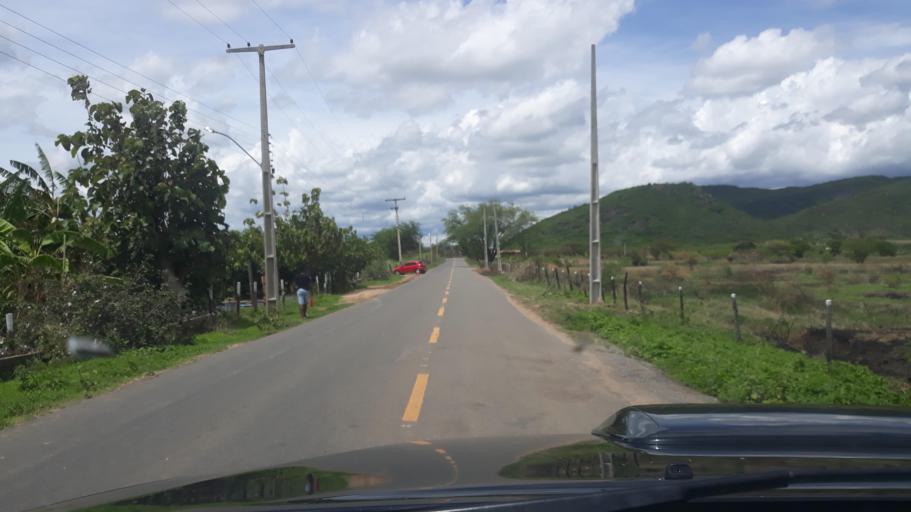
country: BR
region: Bahia
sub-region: Guanambi
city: Guanambi
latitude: -14.2801
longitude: -42.7129
